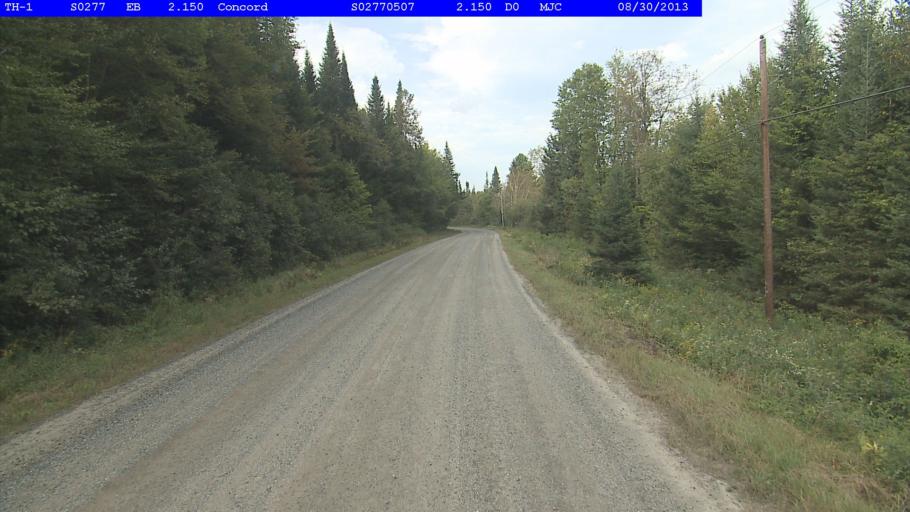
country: US
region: Vermont
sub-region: Caledonia County
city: Lyndonville
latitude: 44.4893
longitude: -71.8552
